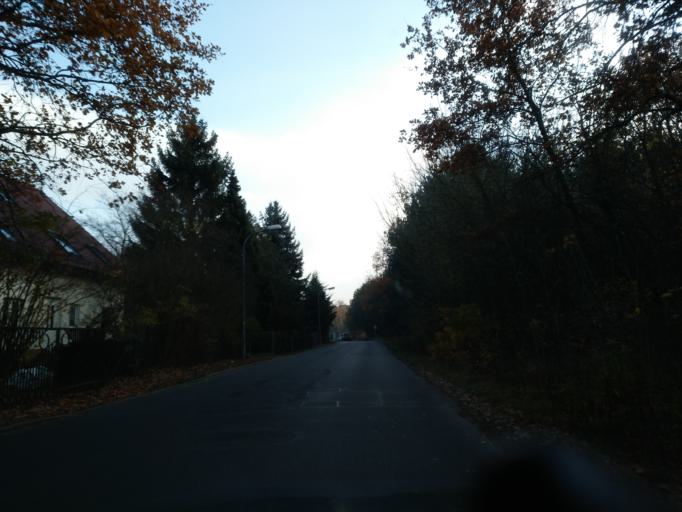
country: DE
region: Berlin
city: Falkenhagener Feld
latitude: 52.5635
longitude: 13.1443
